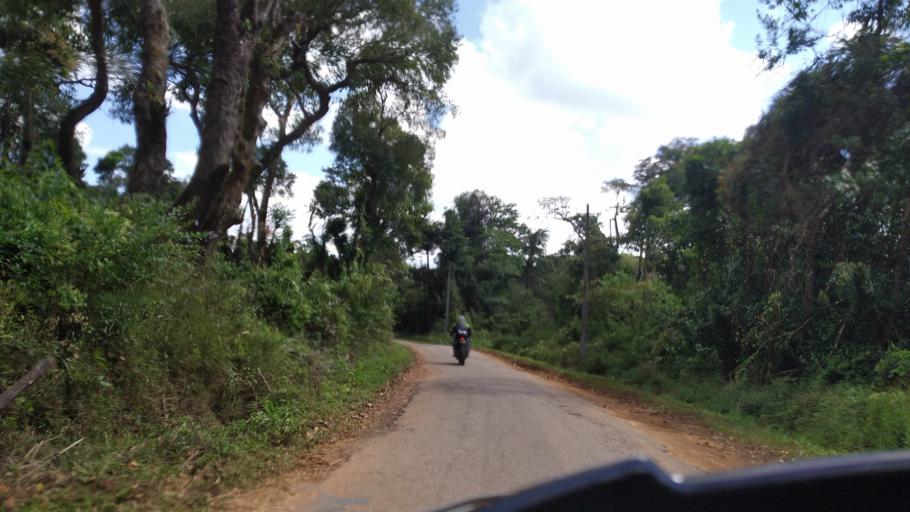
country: IN
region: Karnataka
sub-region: Kodagu
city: Ponnampet
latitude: 12.0246
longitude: 75.8894
